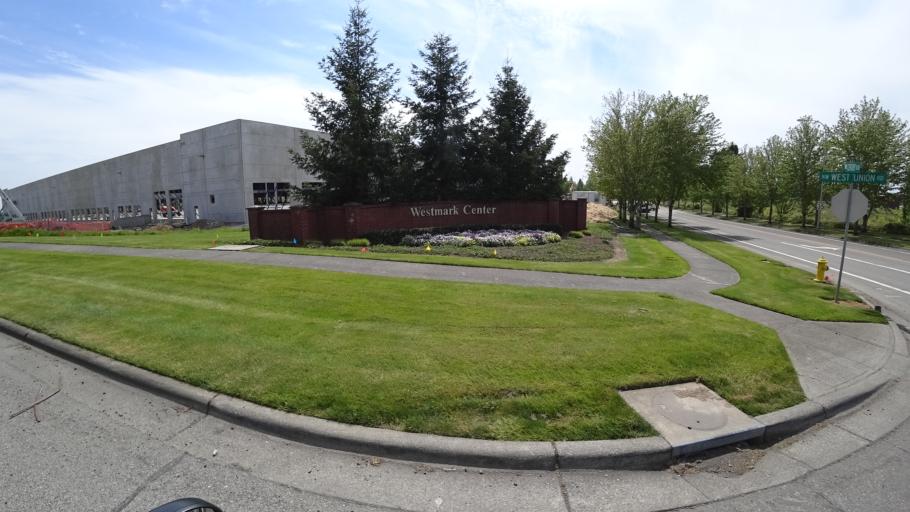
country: US
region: Oregon
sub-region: Washington County
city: Rockcreek
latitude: 45.5734
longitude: -122.9069
